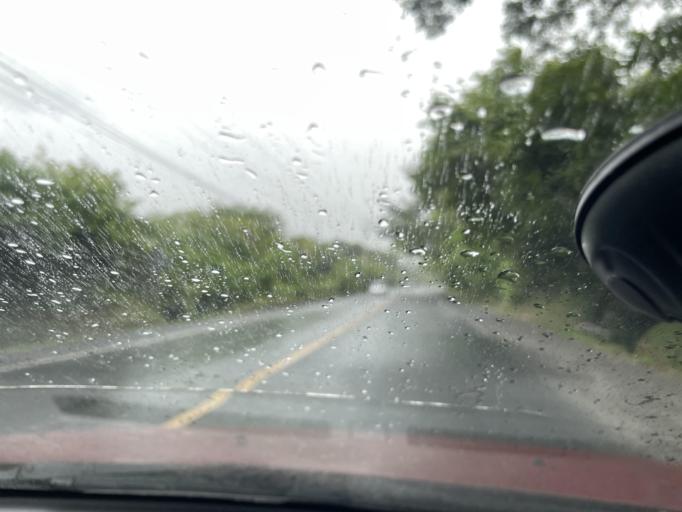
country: SV
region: San Miguel
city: San Miguel
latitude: 13.5327
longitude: -88.1387
